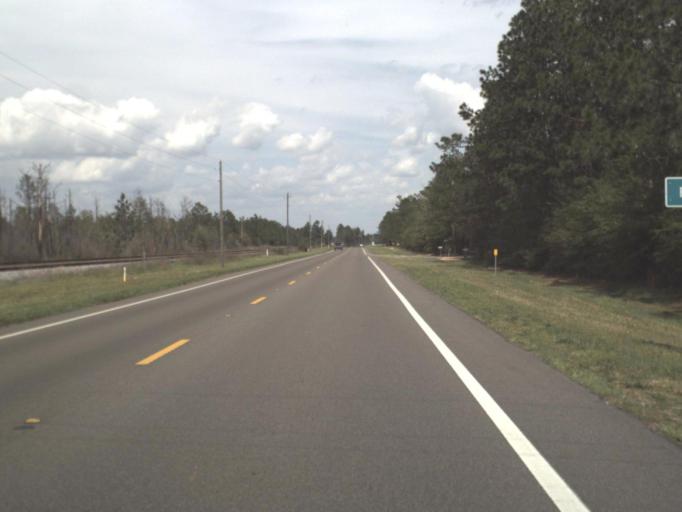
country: US
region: Florida
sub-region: Santa Rosa County
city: East Milton
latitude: 30.6780
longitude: -86.8478
